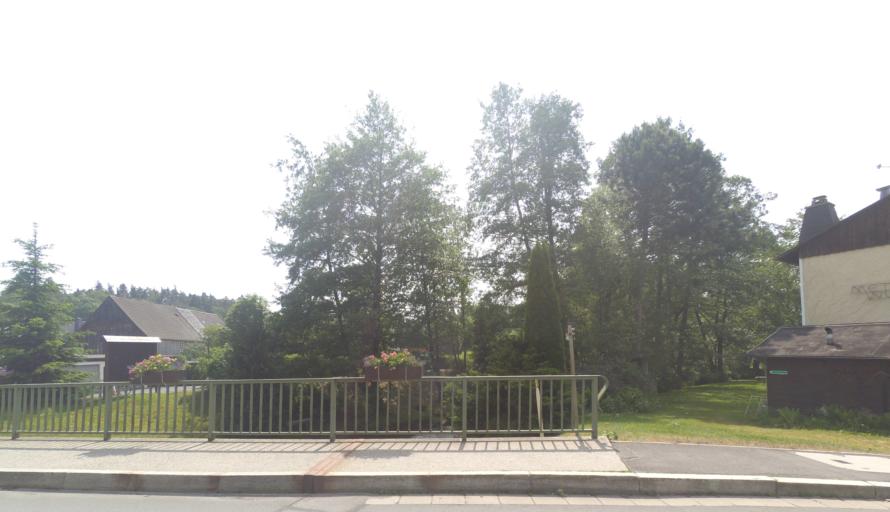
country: DE
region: Bavaria
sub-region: Upper Franconia
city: Roslau
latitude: 50.0828
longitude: 11.9769
